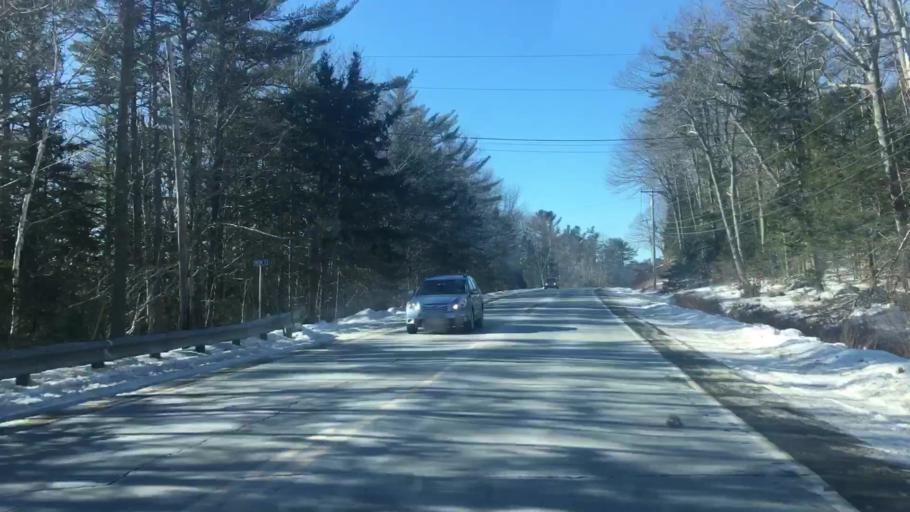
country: US
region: Maine
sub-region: Hancock County
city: Surry
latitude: 44.4947
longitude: -68.4742
